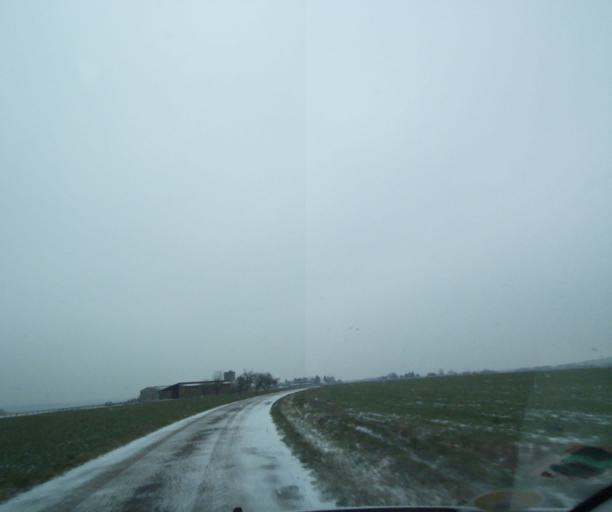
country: FR
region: Champagne-Ardenne
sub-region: Departement de la Haute-Marne
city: Wassy
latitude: 48.4667
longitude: 5.0010
